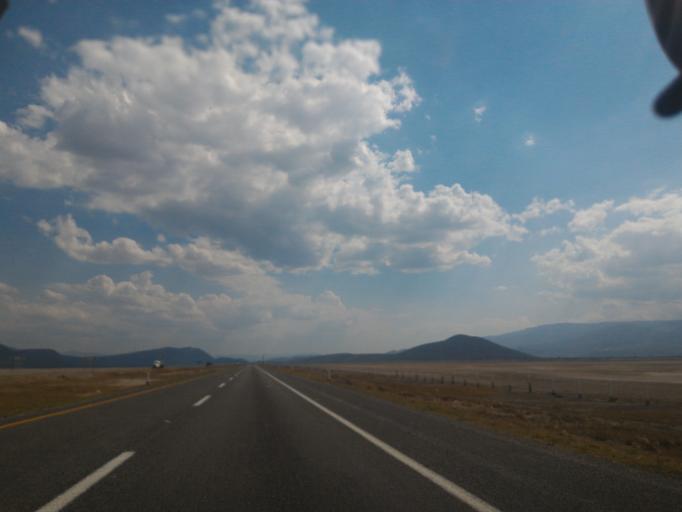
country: MX
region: Jalisco
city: Zacoalco de Torres
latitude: 20.3089
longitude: -103.5616
